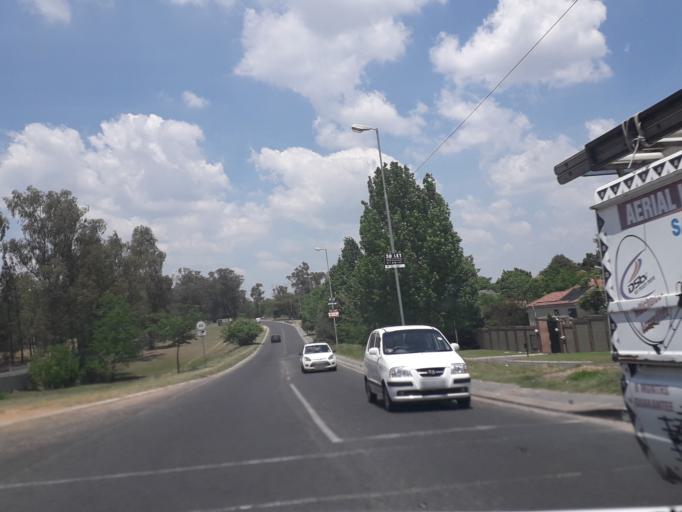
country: ZA
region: Gauteng
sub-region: City of Johannesburg Metropolitan Municipality
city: Midrand
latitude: -26.0423
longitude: 28.0697
